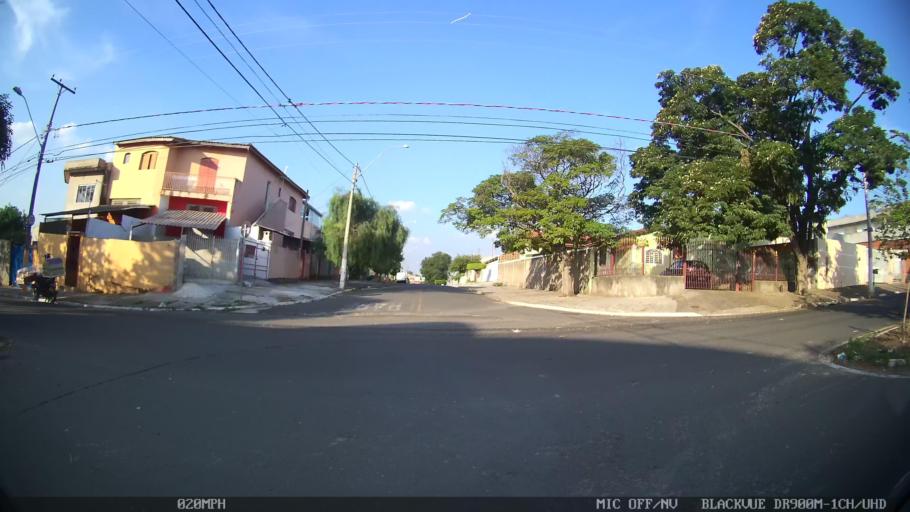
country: BR
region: Sao Paulo
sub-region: Campinas
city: Campinas
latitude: -22.9704
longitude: -47.1227
